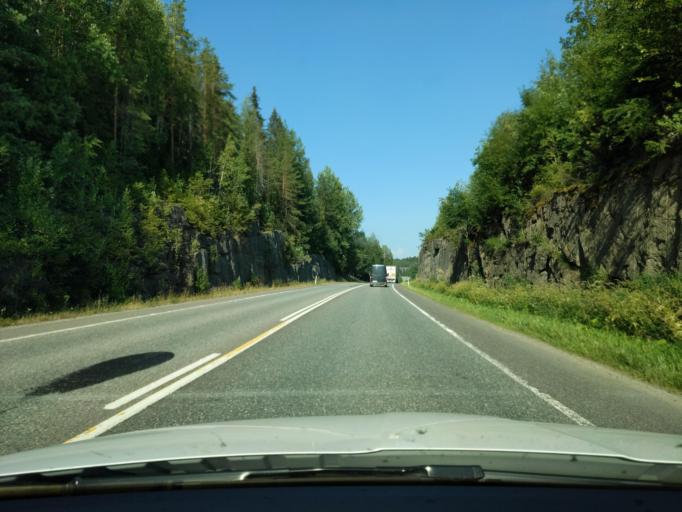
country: FI
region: Paijanne Tavastia
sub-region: Lahti
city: Hollola
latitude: 60.9626
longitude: 25.4515
